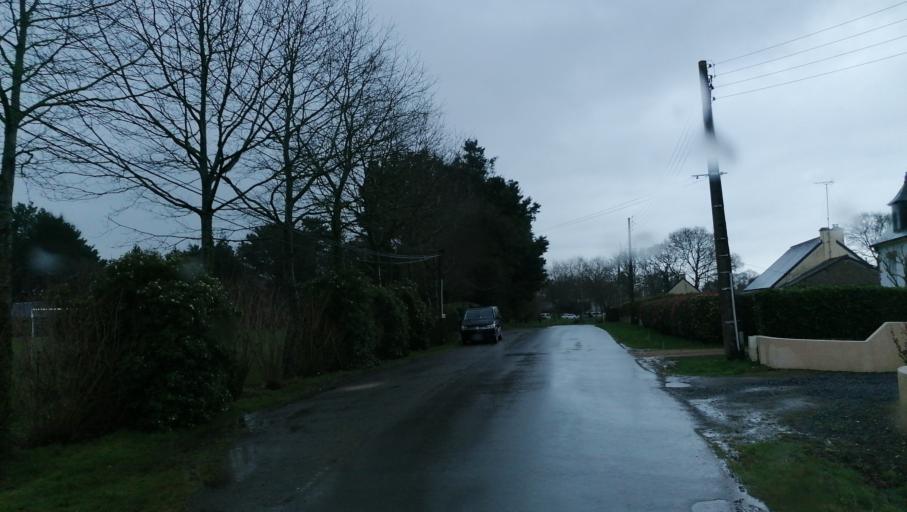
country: FR
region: Brittany
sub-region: Departement des Cotes-d'Armor
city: Plouagat
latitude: 48.4866
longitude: -2.9619
